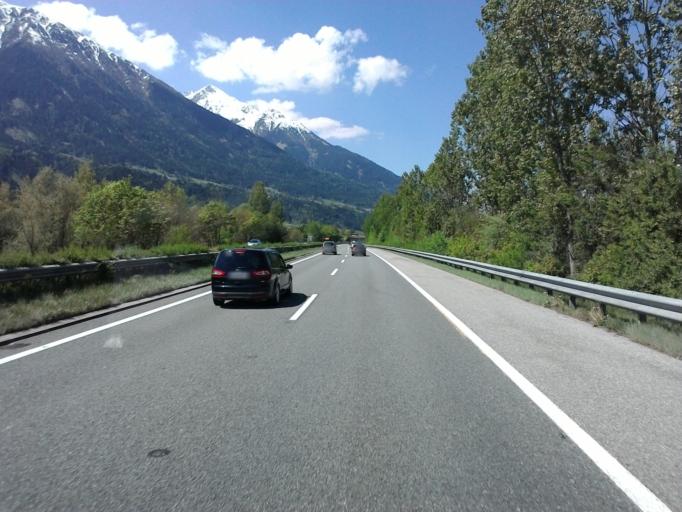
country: AT
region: Tyrol
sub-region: Politischer Bezirk Innsbruck Land
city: Inzing
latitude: 47.2861
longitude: 11.1782
